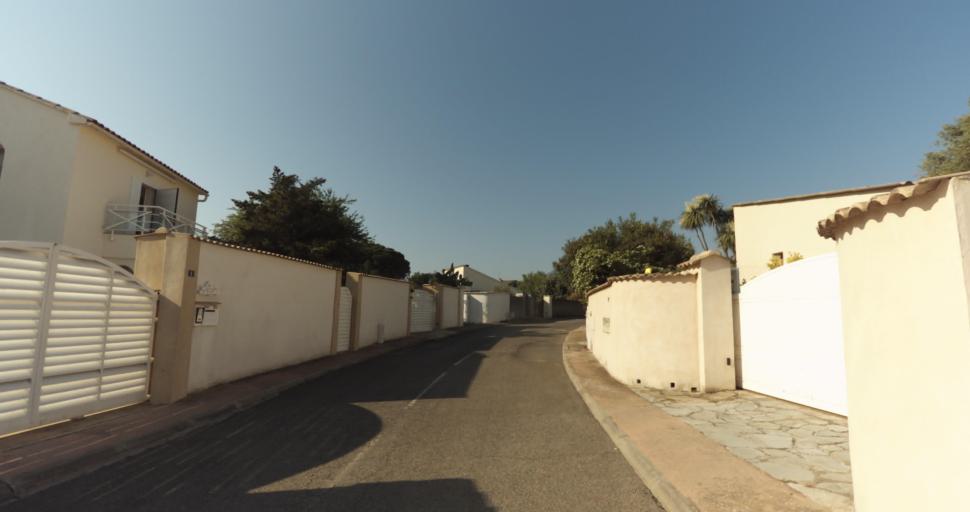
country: FR
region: Corsica
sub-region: Departement de la Haute-Corse
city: Biguglia
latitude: 42.6365
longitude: 9.4321
